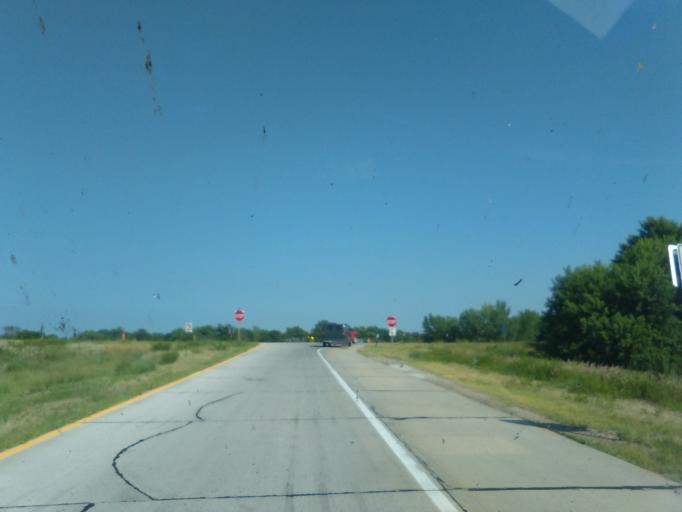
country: US
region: Nebraska
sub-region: Hall County
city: Grand Island
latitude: 40.8186
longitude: -98.3793
